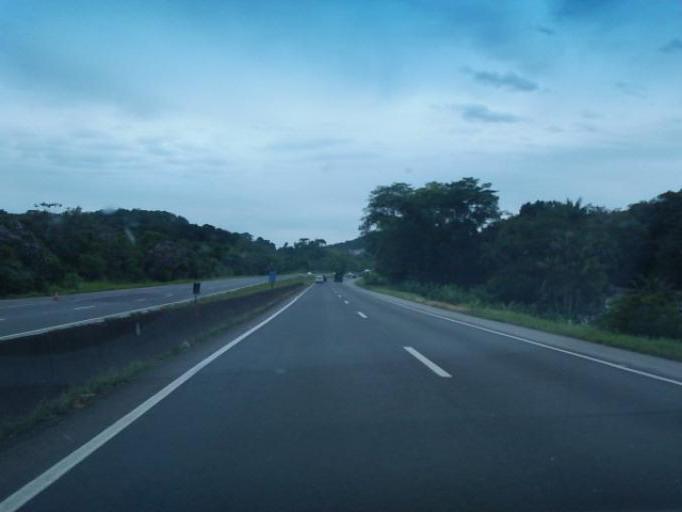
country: BR
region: Sao Paulo
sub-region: Juquia
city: Juquia
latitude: -24.3688
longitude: -47.6965
